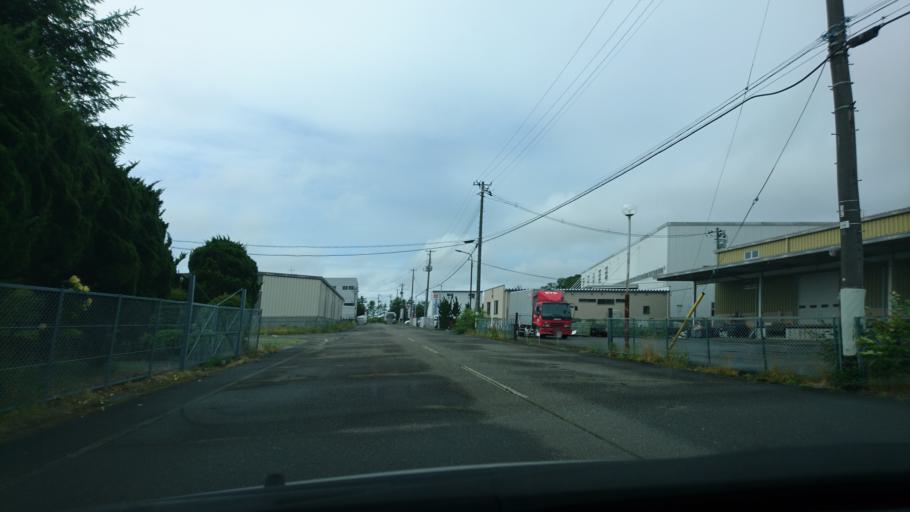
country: JP
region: Iwate
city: Ichinoseki
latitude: 38.9054
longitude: 141.1601
